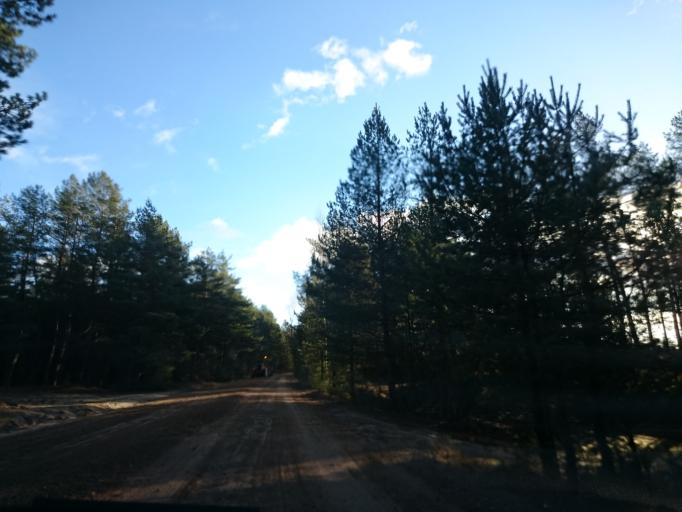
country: LV
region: Garkalne
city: Garkalne
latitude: 57.0597
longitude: 24.4145
